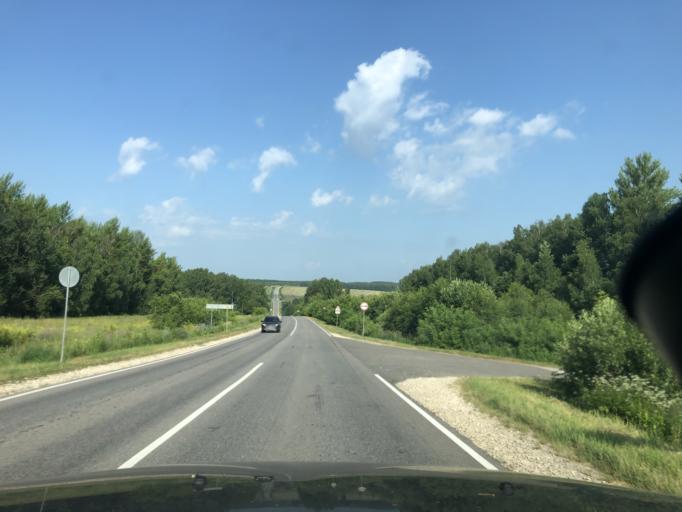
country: RU
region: Tula
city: Dubna
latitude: 54.1280
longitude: 37.0586
